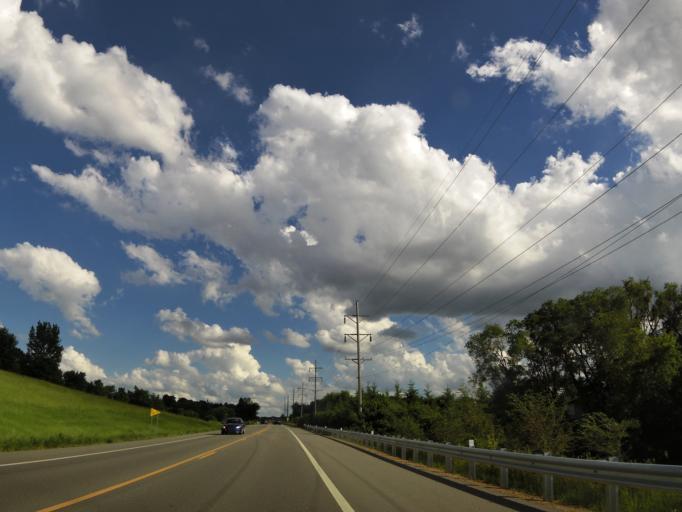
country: US
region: Minnesota
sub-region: Carver County
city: Waconia
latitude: 44.8839
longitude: -93.8157
